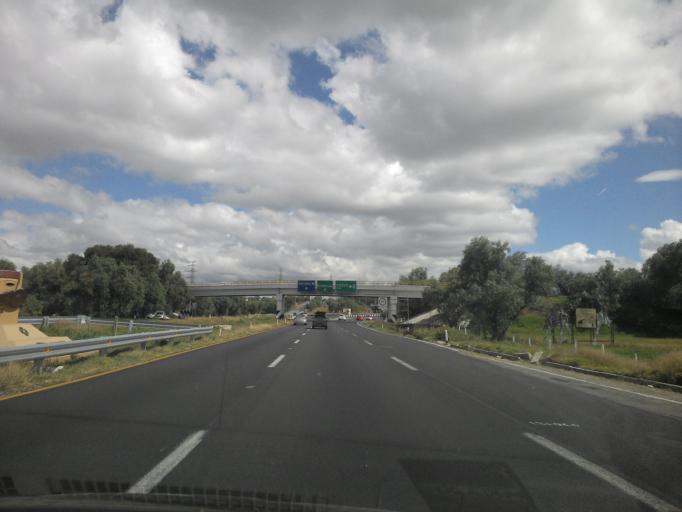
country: MX
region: Morelos
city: Xometla
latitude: 19.6533
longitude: -98.8817
